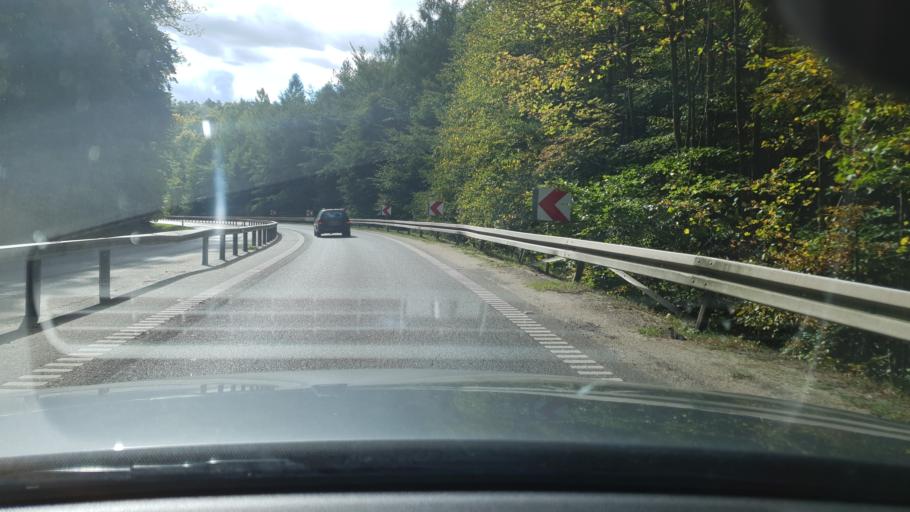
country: PL
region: Pomeranian Voivodeship
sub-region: Powiat wejherowski
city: Rekowo Dolne
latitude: 54.6273
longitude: 18.3427
